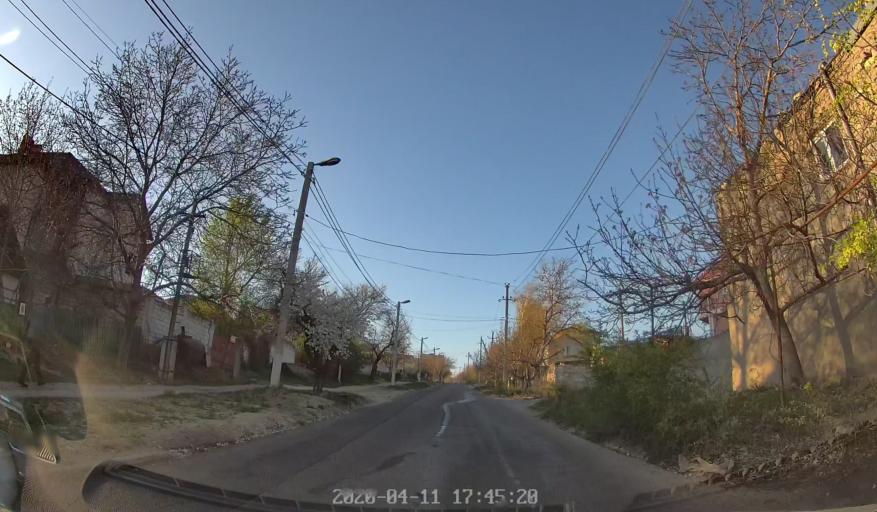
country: MD
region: Chisinau
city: Chisinau
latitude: 46.9842
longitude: 28.8227
